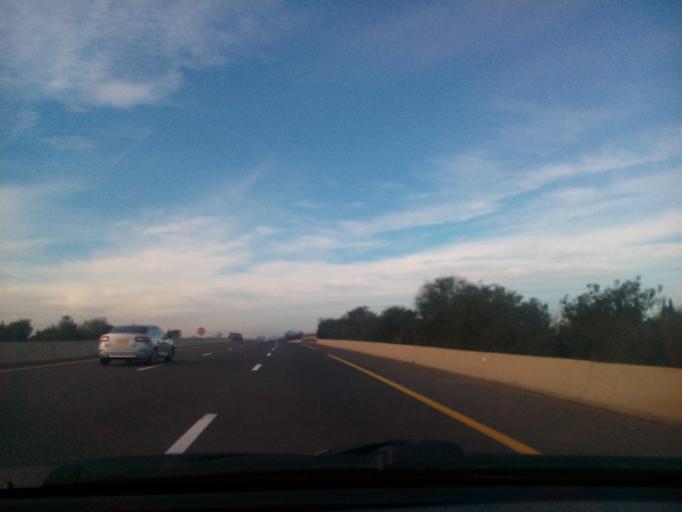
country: DZ
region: Mascara
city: Mascara
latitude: 35.6212
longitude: 0.0474
